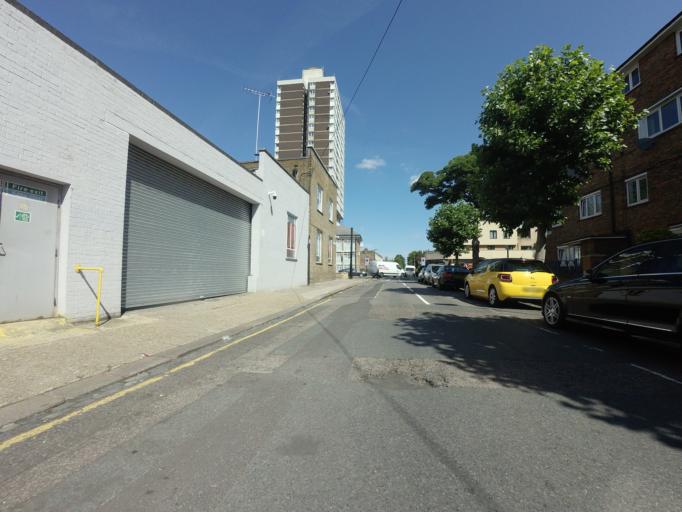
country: GB
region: England
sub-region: Greater London
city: East Ham
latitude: 51.5434
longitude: 0.0131
